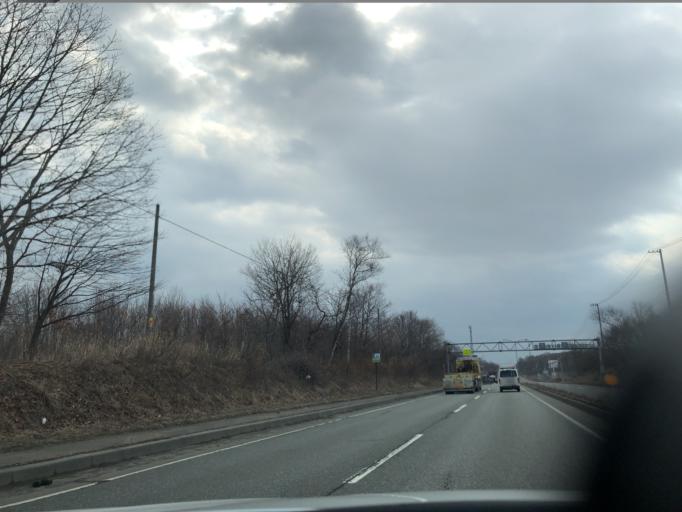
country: JP
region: Hokkaido
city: Chitose
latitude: 42.7823
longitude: 141.7019
